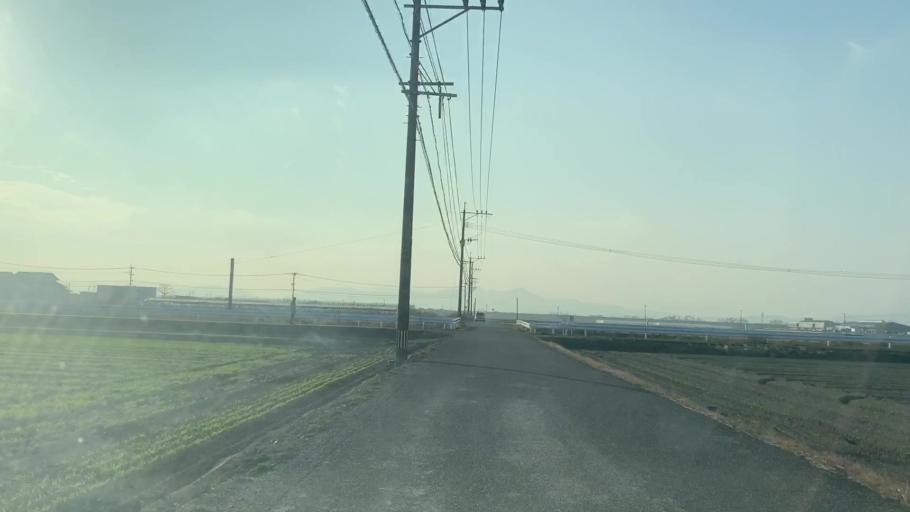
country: JP
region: Saga Prefecture
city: Saga-shi
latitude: 33.2605
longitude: 130.2555
